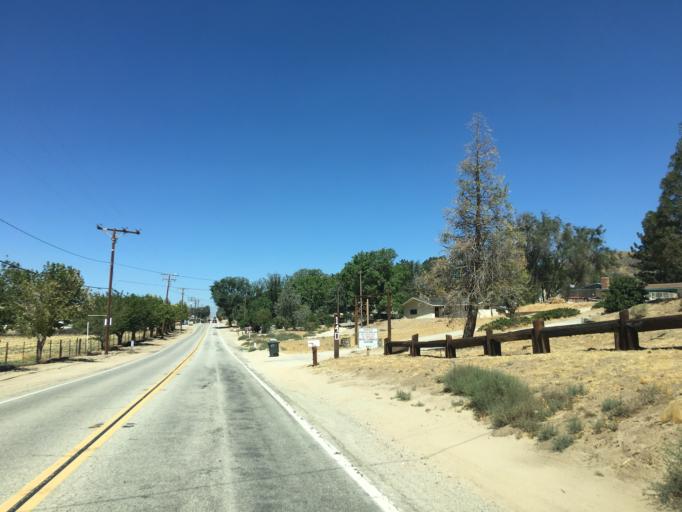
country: US
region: California
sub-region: Los Angeles County
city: Leona Valley
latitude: 34.6167
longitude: -118.2847
